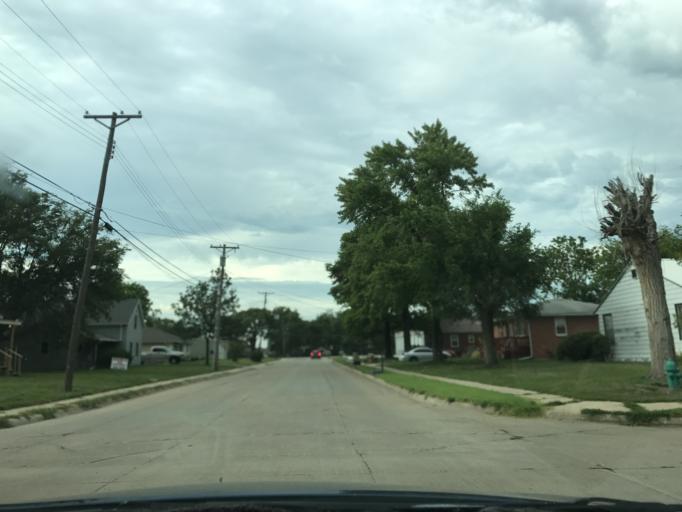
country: US
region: Nebraska
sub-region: Gage County
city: Beatrice
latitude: 40.2641
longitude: -96.7786
